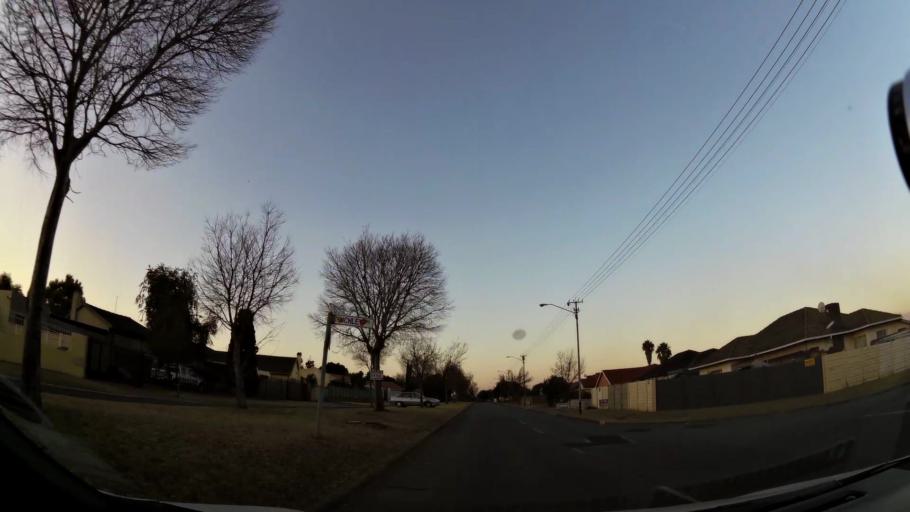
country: ZA
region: Gauteng
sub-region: Ekurhuleni Metropolitan Municipality
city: Germiston
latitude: -26.2664
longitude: 28.1590
